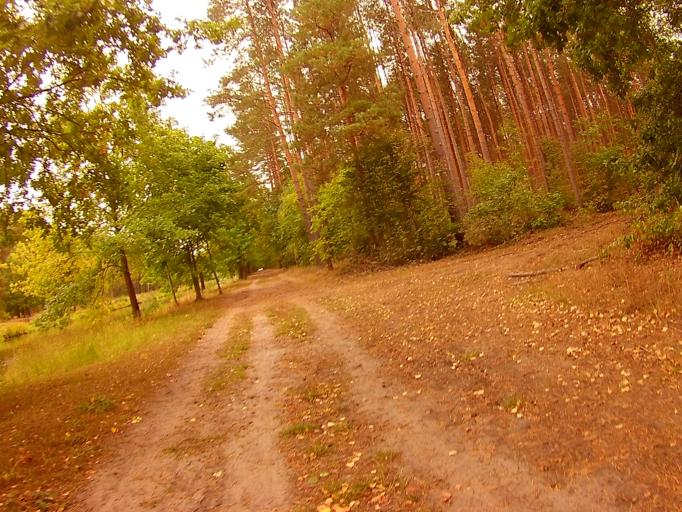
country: DE
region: Berlin
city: Schmockwitz
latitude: 52.3757
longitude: 13.6893
